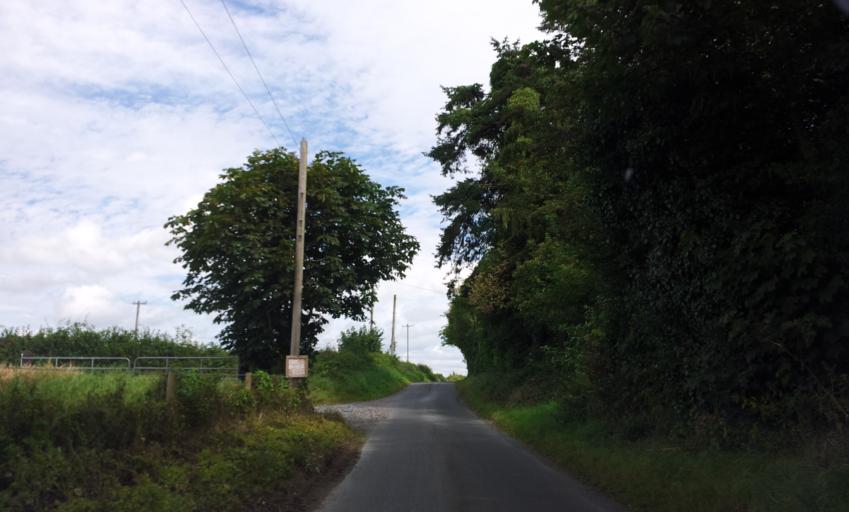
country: IE
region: Leinster
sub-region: Laois
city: Stradbally
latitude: 53.0141
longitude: -7.1953
